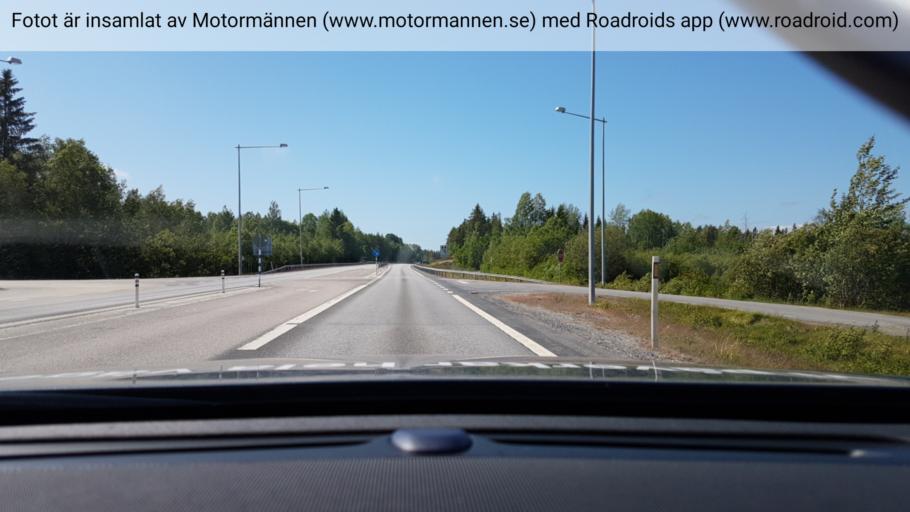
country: SE
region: Vaesterbotten
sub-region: Umea Kommun
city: Roback
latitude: 63.7548
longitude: 20.1563
